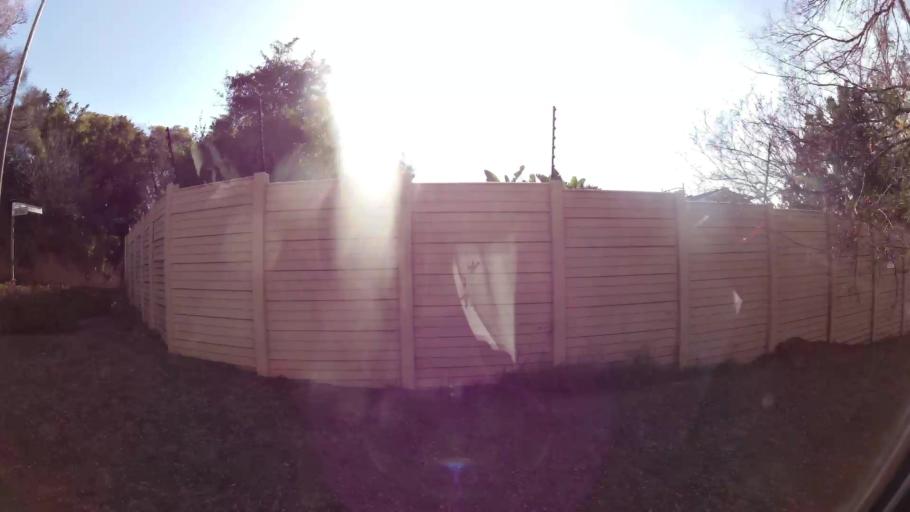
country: ZA
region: Gauteng
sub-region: City of Johannesburg Metropolitan Municipality
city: Johannesburg
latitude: -26.0965
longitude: 27.9798
